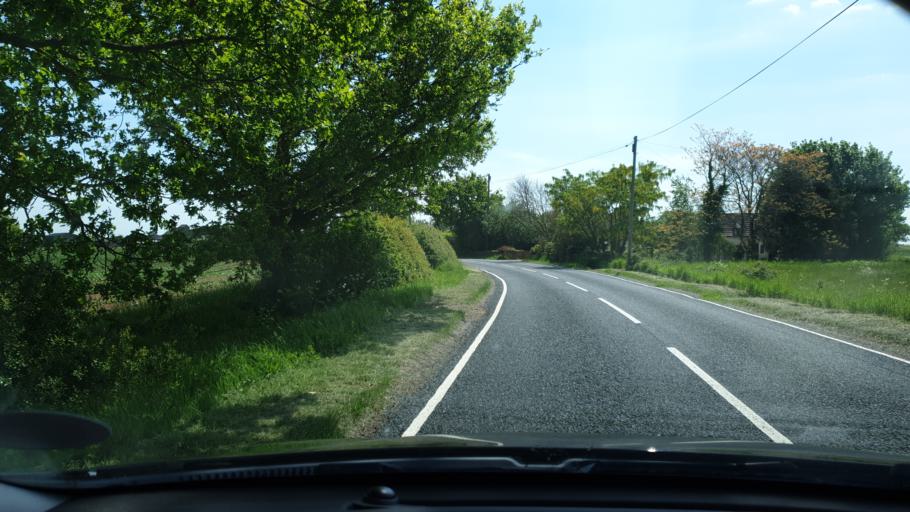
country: GB
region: England
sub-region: Essex
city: Manningtree
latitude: 51.9032
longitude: 1.0605
